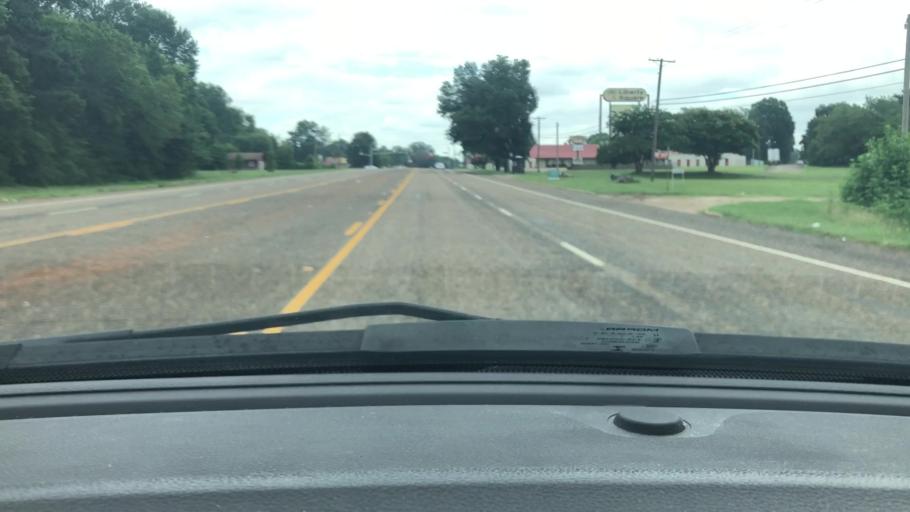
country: US
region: Texas
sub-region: Bowie County
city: Wake Village
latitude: 33.3999
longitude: -94.0835
